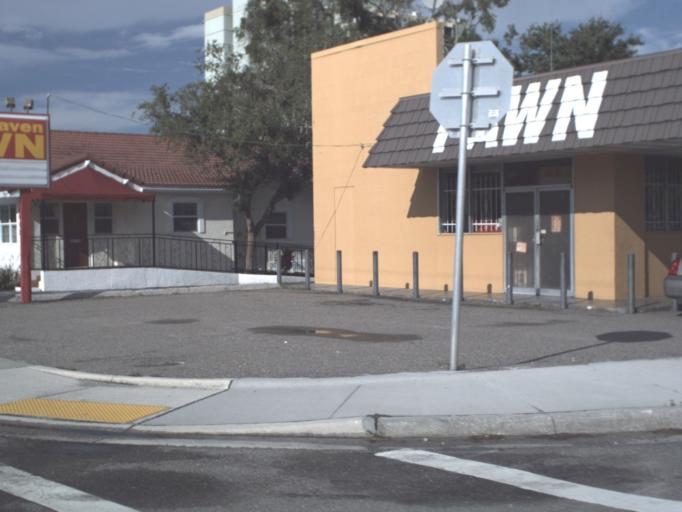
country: US
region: Florida
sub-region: Polk County
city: Winter Haven
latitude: 28.0315
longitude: -81.7329
